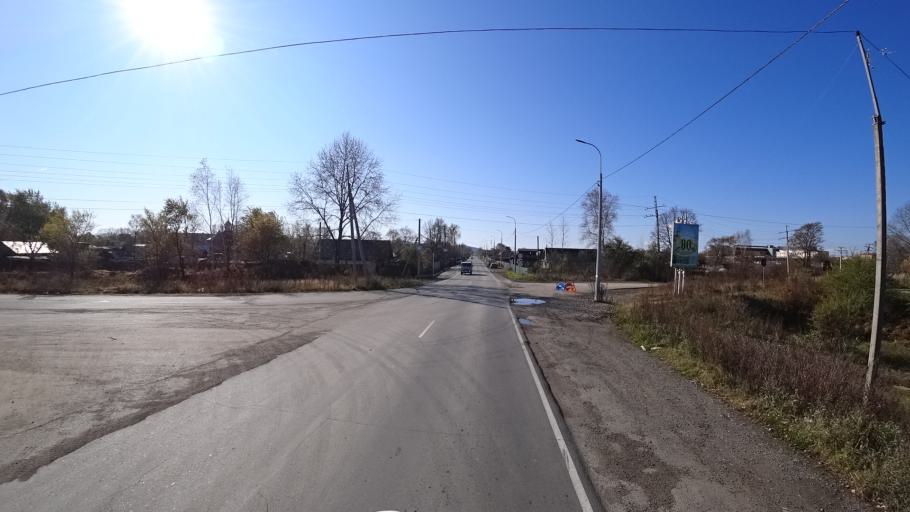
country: RU
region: Khabarovsk Krai
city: Amursk
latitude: 50.1055
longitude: 136.5132
